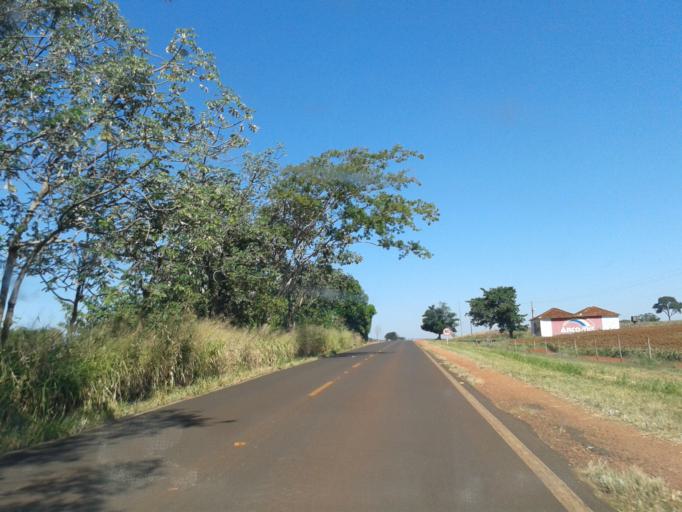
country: BR
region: Minas Gerais
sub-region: Capinopolis
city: Capinopolis
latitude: -18.5883
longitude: -49.5152
